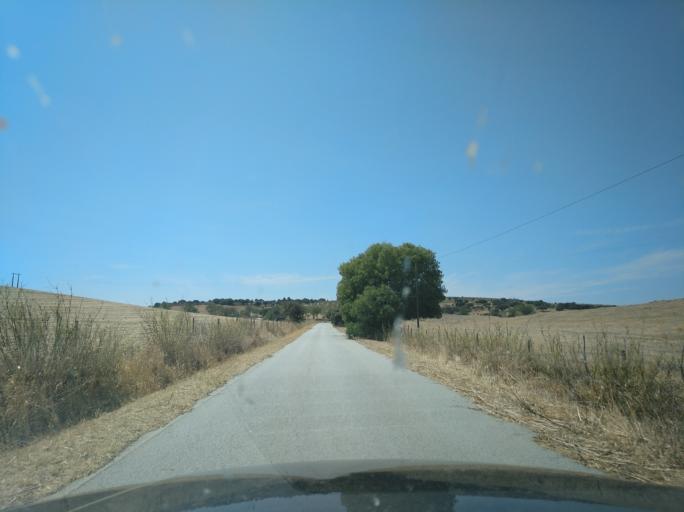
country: PT
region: Portalegre
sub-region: Campo Maior
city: Campo Maior
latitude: 38.9618
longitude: -7.1181
